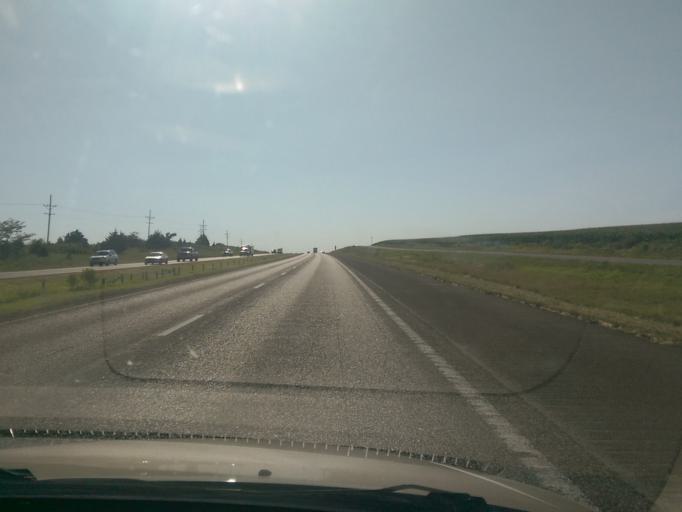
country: US
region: Missouri
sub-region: Lafayette County
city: Concordia
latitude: 38.9877
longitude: -93.5128
